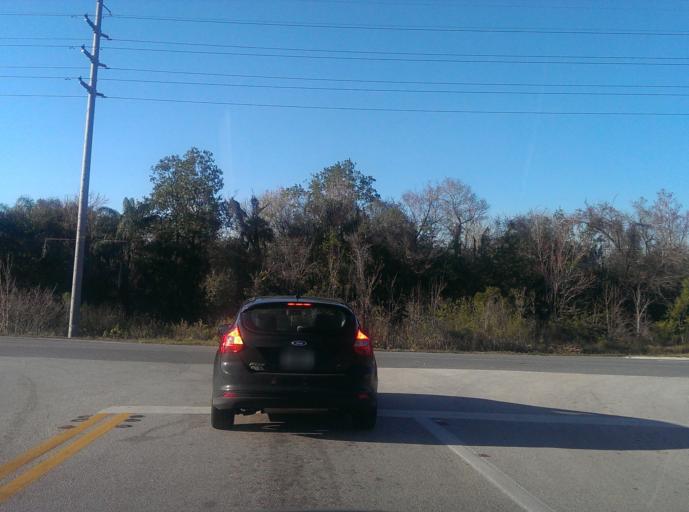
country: US
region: Florida
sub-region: Polk County
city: Loughman
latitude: 28.2600
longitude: -81.5801
